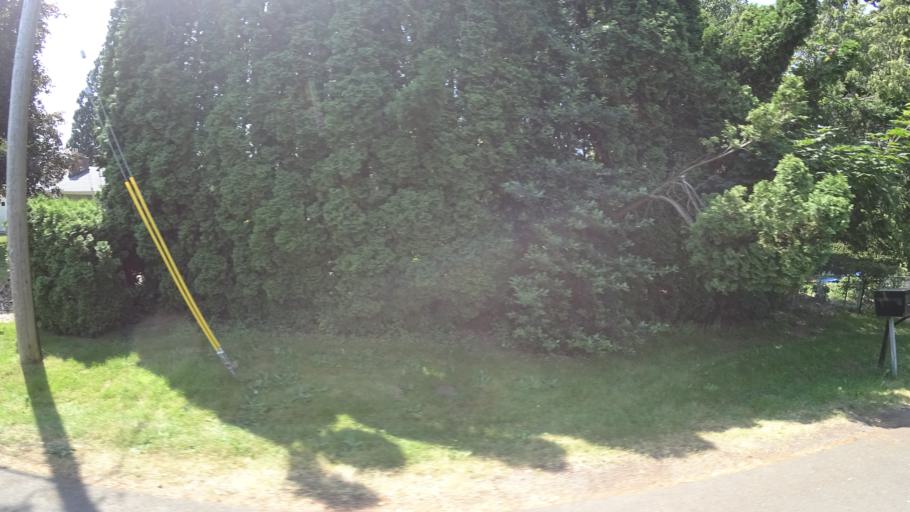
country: US
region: Oregon
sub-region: Clackamas County
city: Oatfield
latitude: 45.4458
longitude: -122.5988
